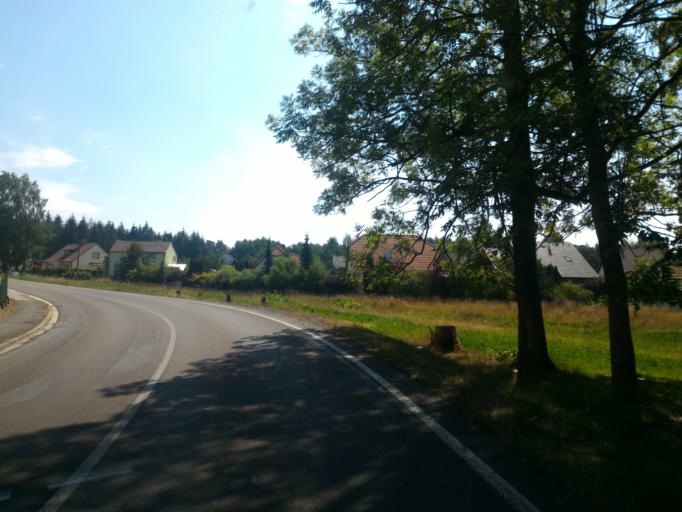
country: CZ
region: Pardubicky
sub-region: Okres Chrudim
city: Hlinsko
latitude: 49.7695
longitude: 15.8544
